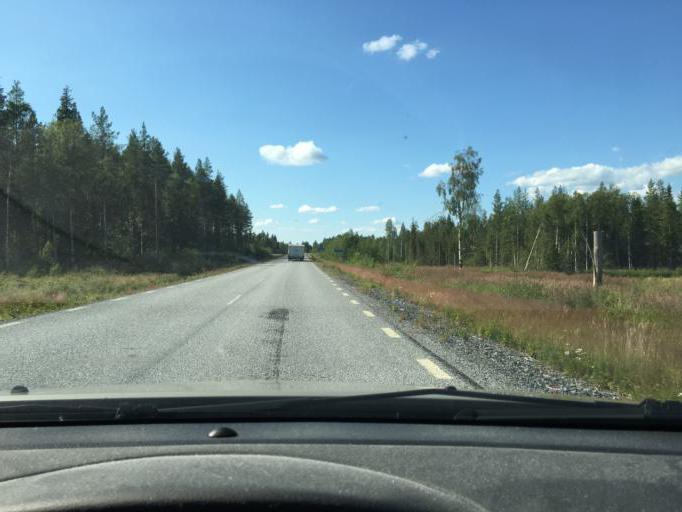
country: SE
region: Norrbotten
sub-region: Lulea Kommun
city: Ranea
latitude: 66.0408
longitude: 22.3038
